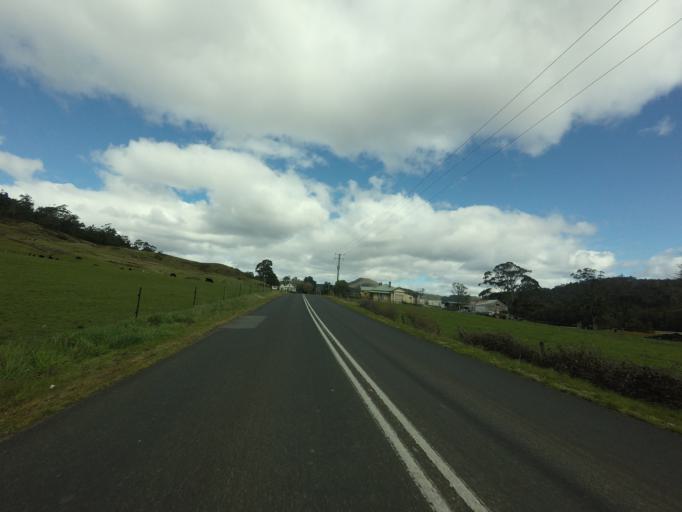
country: AU
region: Tasmania
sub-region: Huon Valley
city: Geeveston
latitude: -43.1832
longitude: 146.9297
